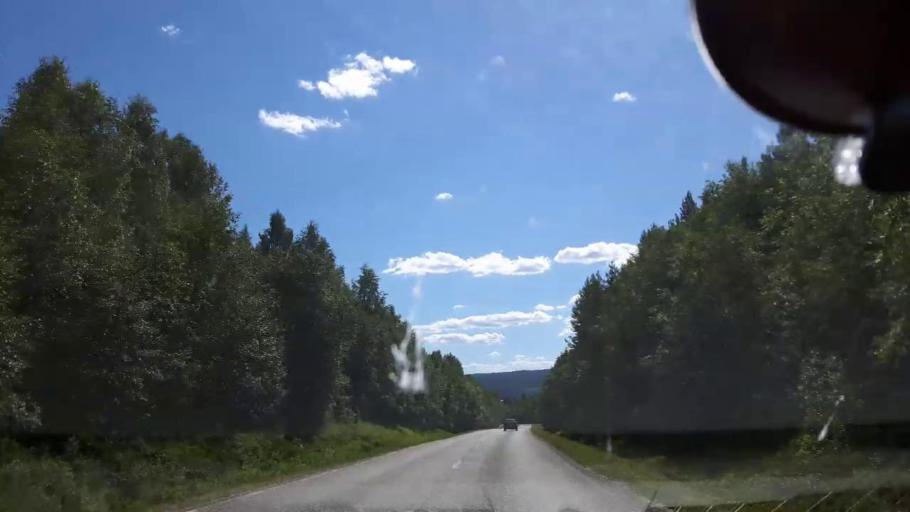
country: SE
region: Vaesternorrland
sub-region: Ange Kommun
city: Fransta
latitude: 62.8056
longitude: 16.2098
